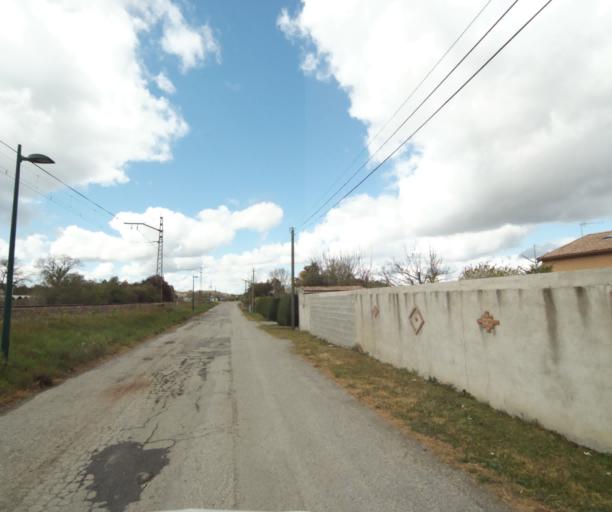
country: FR
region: Midi-Pyrenees
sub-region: Departement de l'Ariege
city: Saverdun
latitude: 43.2360
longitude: 1.5844
